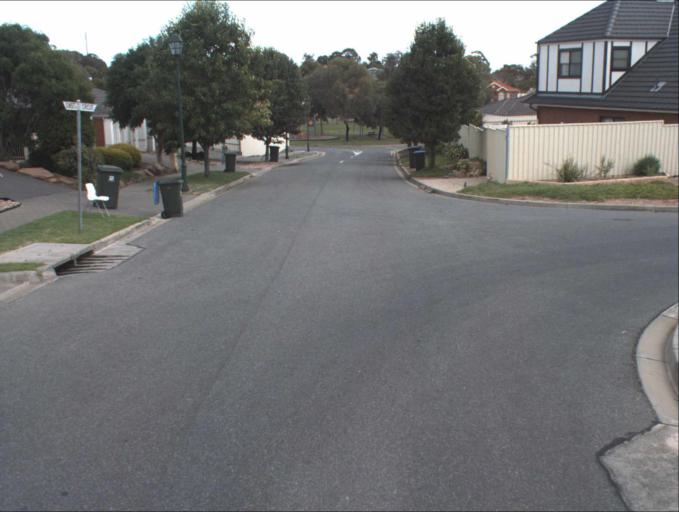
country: AU
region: South Australia
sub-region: Port Adelaide Enfield
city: Gilles Plains
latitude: -34.8449
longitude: 138.6469
